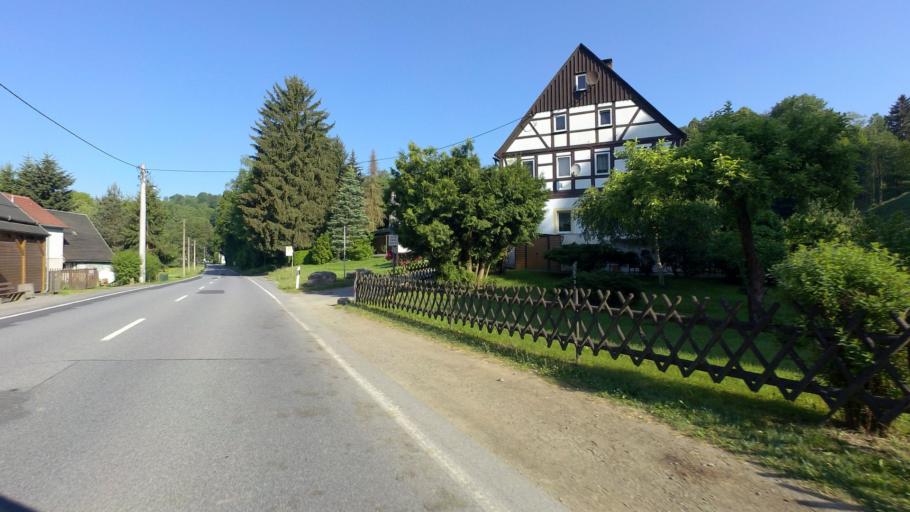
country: DE
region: Saxony
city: Sebnitz
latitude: 50.9676
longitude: 14.2414
